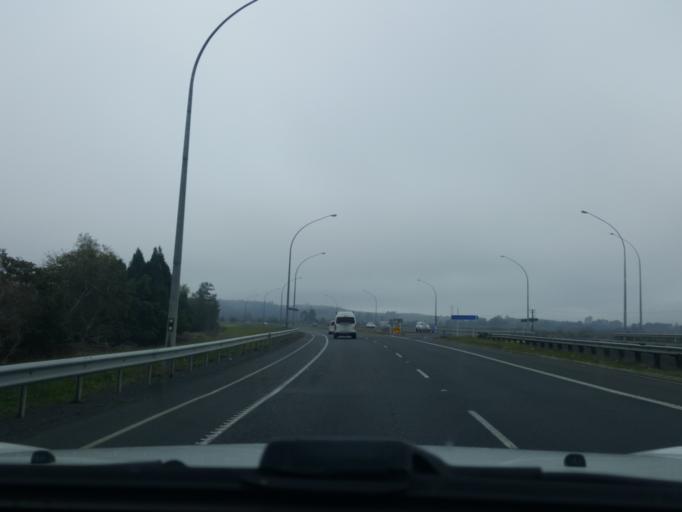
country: NZ
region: Waikato
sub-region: Waikato District
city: Te Kauwhata
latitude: -37.3100
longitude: 175.0673
